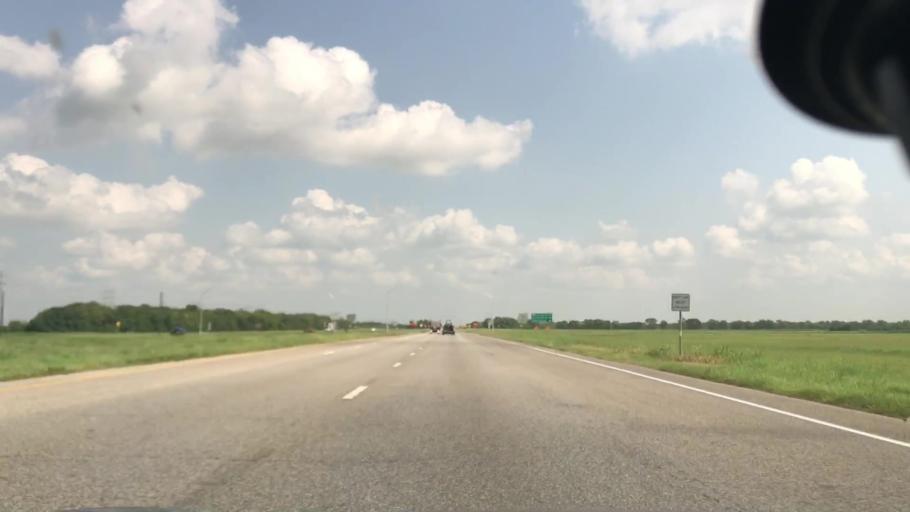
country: US
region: Texas
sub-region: Brazoria County
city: Rosharon
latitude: 29.3794
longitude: -95.4265
